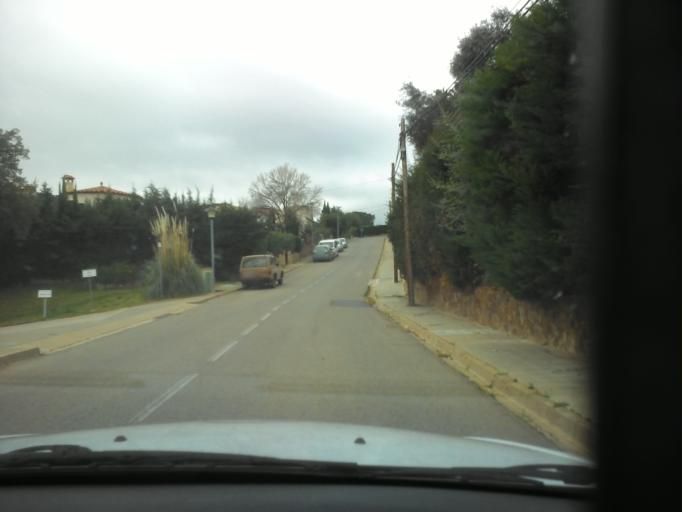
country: ES
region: Catalonia
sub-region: Provincia de Girona
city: Calonge
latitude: 41.8534
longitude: 3.0594
